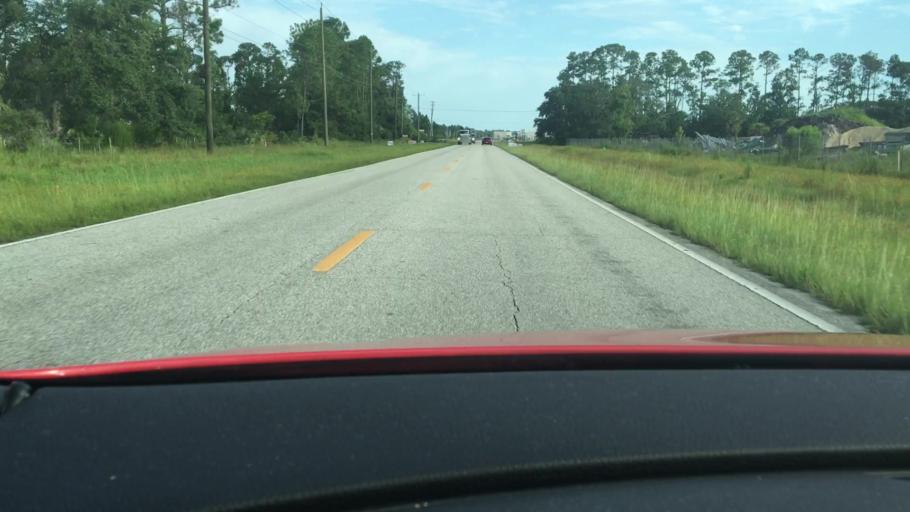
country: US
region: Florida
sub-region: Volusia County
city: Daytona Beach
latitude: 29.1818
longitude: -81.0923
